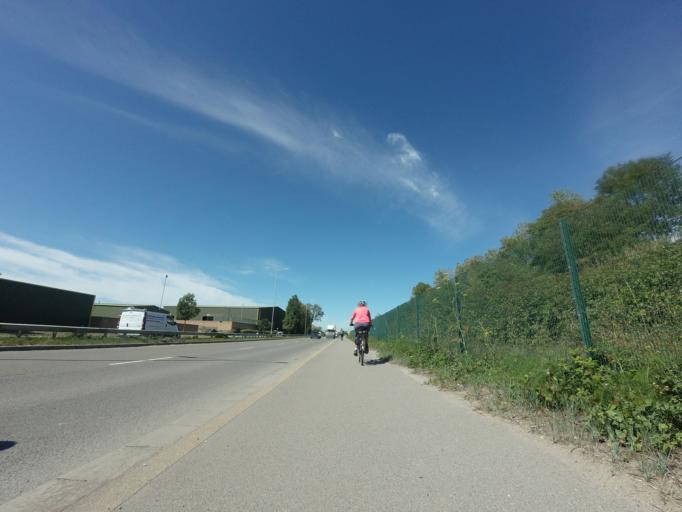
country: GB
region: England
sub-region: Kent
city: Sandwich
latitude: 51.2997
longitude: 1.3471
